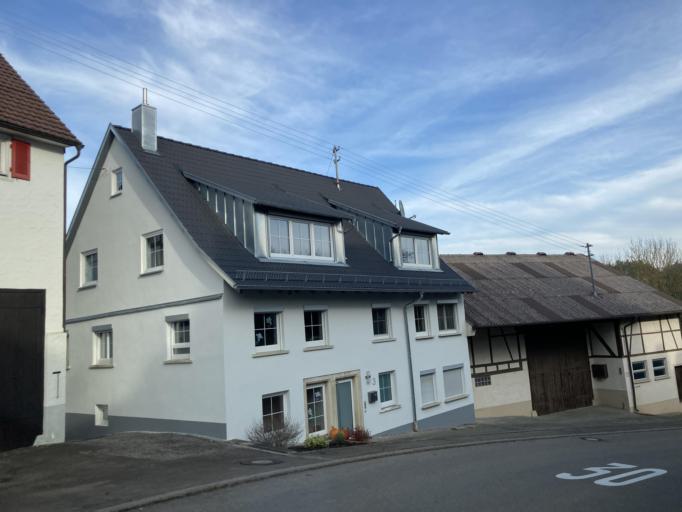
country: DE
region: Baden-Wuerttemberg
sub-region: Tuebingen Region
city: Hirrlingen
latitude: 48.4116
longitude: 8.8675
